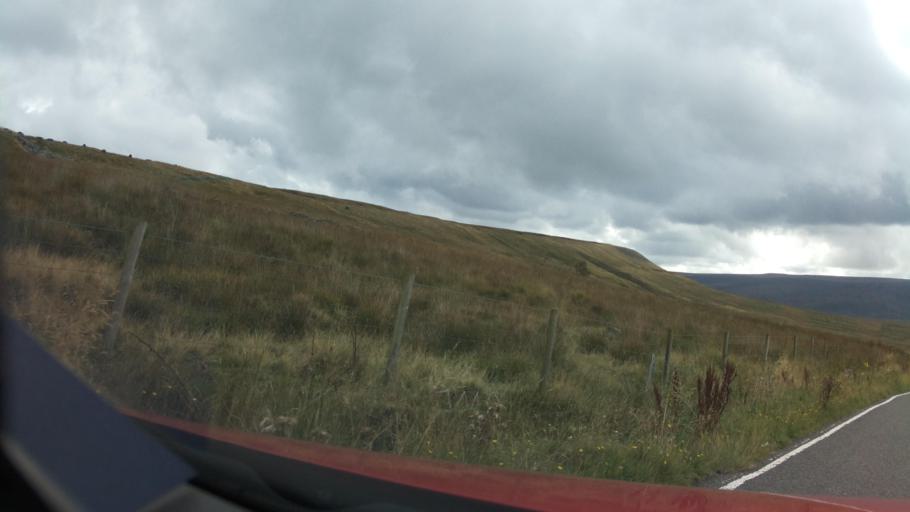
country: GB
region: England
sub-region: Kirklees
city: Meltham
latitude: 53.5189
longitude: -1.8509
